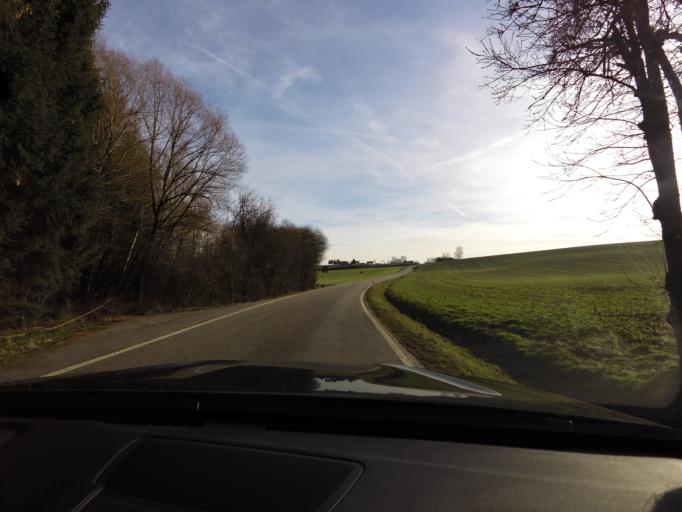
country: DE
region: Bavaria
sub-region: Lower Bavaria
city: Vilsheim
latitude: 48.4629
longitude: 12.1057
